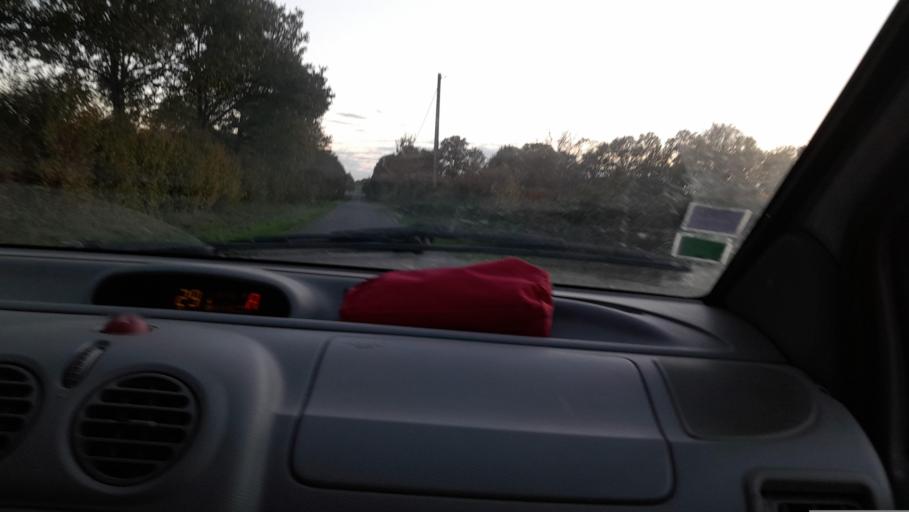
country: FR
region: Brittany
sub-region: Departement d'Ille-et-Vilaine
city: La Guerche-de-Bretagne
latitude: 47.9015
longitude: -1.1610
